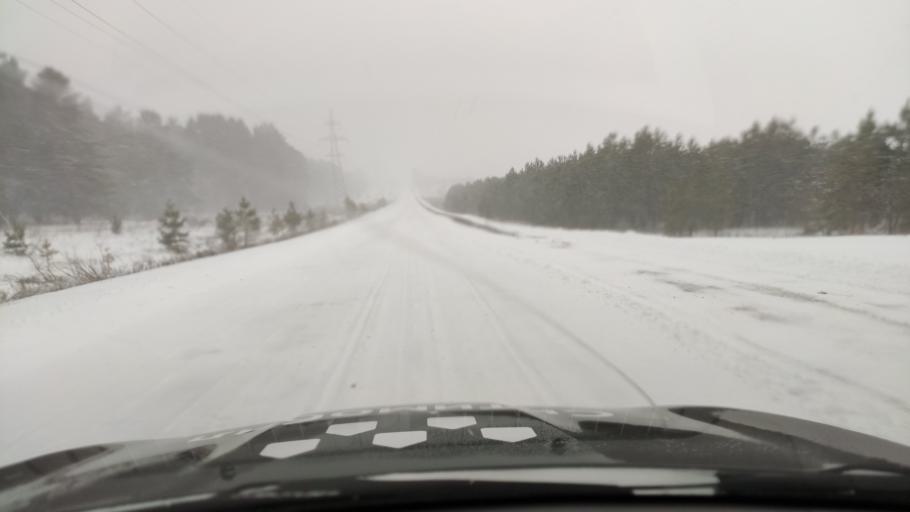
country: RU
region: Samara
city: Povolzhskiy
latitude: 53.5225
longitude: 49.7000
